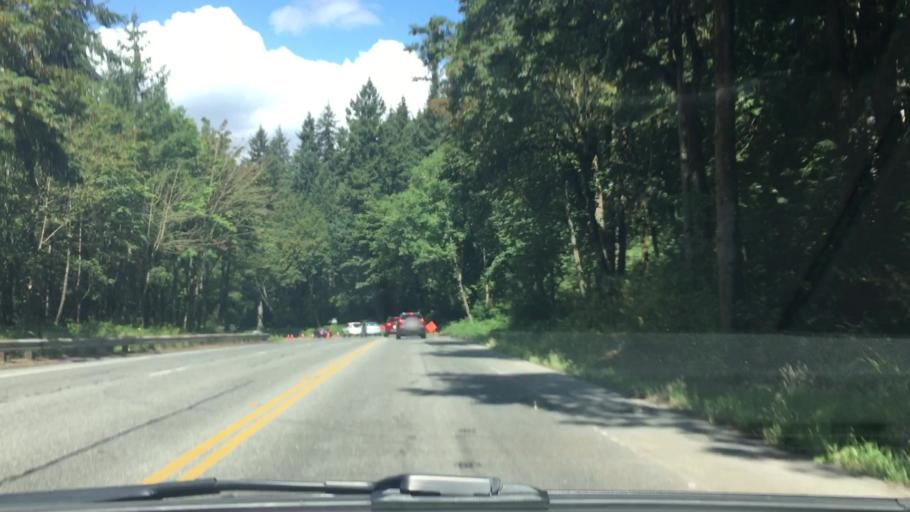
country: US
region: Washington
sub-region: King County
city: City of Sammamish
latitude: 47.5699
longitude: -122.0485
